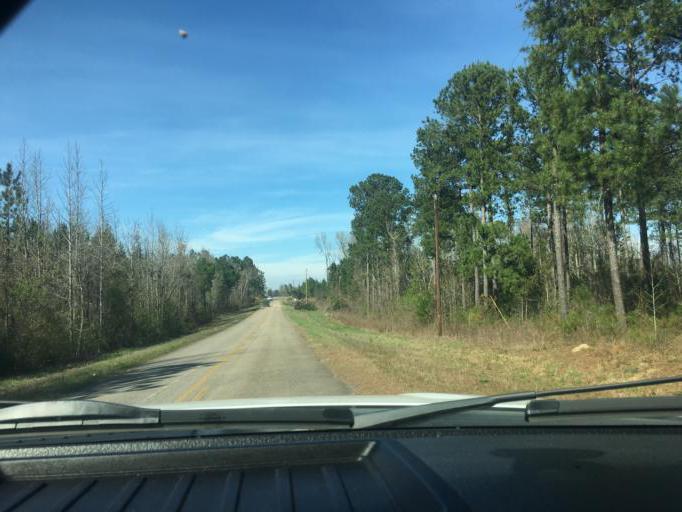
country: US
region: Alabama
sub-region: Lee County
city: Auburn
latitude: 32.4594
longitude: -85.4024
